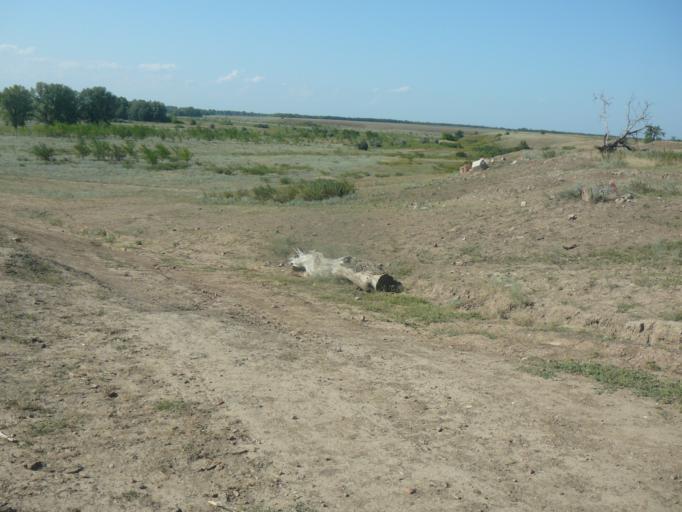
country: RU
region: Saratov
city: Krasnyy Yar
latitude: 51.5676
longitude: 46.5273
